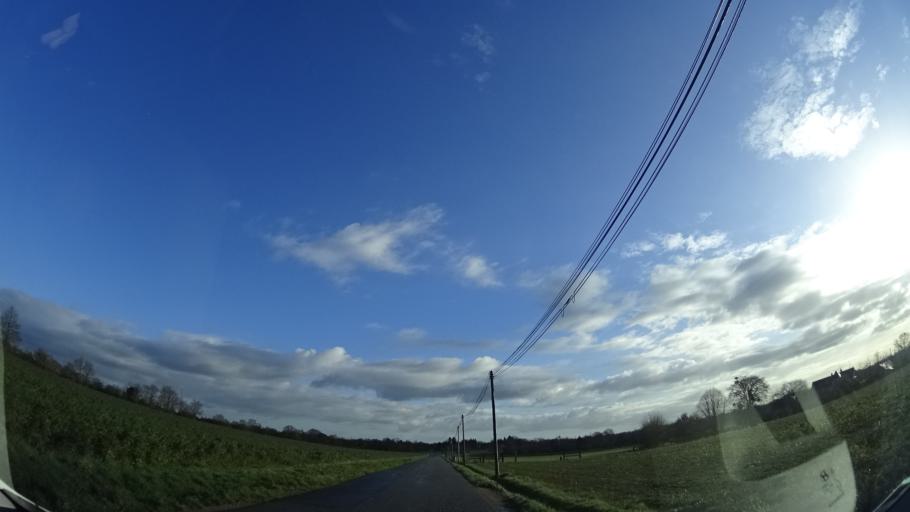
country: FR
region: Brittany
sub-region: Departement d'Ille-et-Vilaine
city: Chantepie
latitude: 48.0868
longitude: -1.5949
